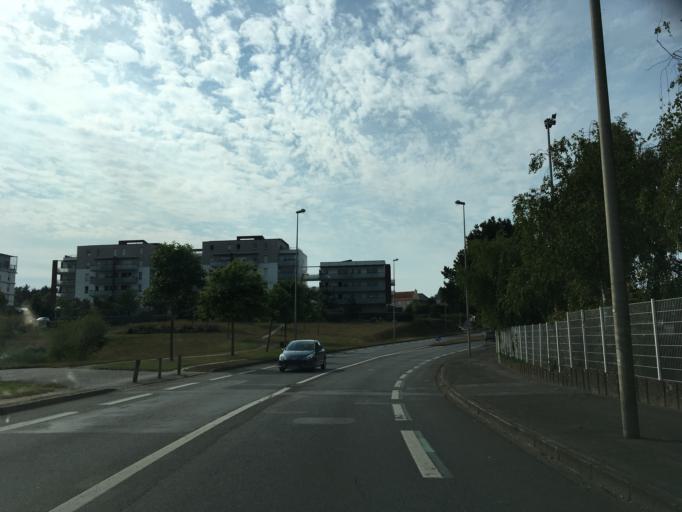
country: FR
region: Brittany
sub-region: Departement du Morbihan
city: Lorient
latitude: 47.7530
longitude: -3.3824
